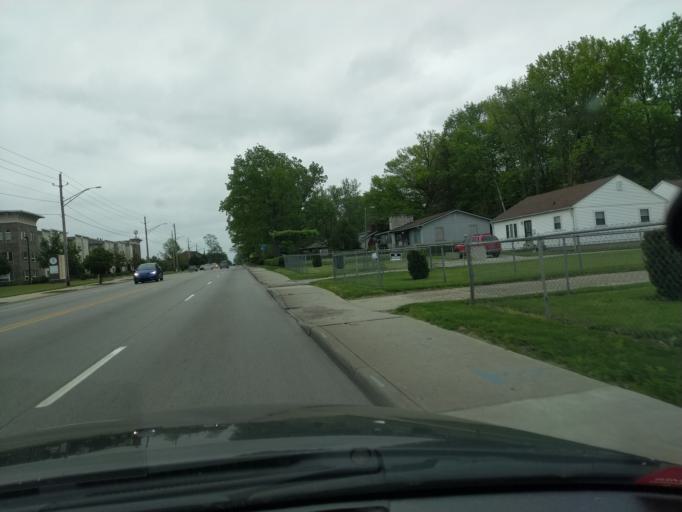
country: US
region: Indiana
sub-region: Marion County
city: Broad Ripple
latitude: 39.8253
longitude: -86.1110
